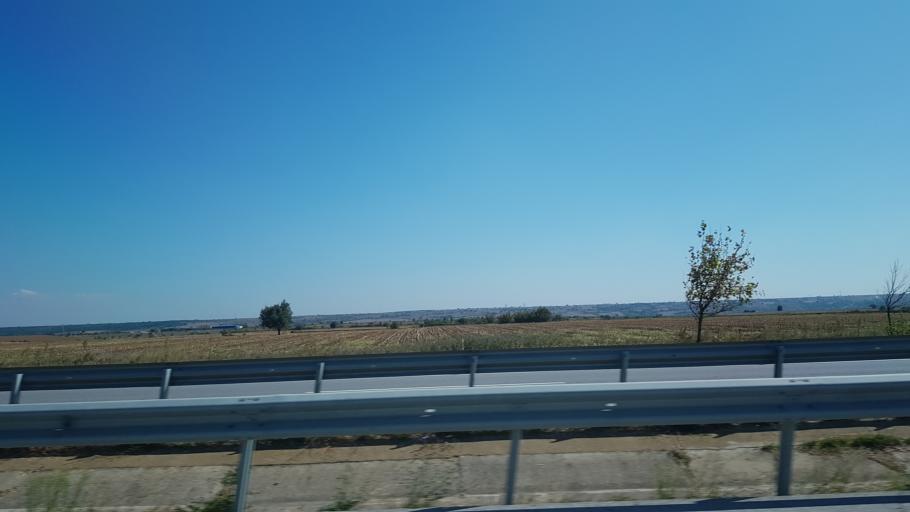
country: TR
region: Kirklareli
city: Babaeski
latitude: 41.5592
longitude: 27.1405
